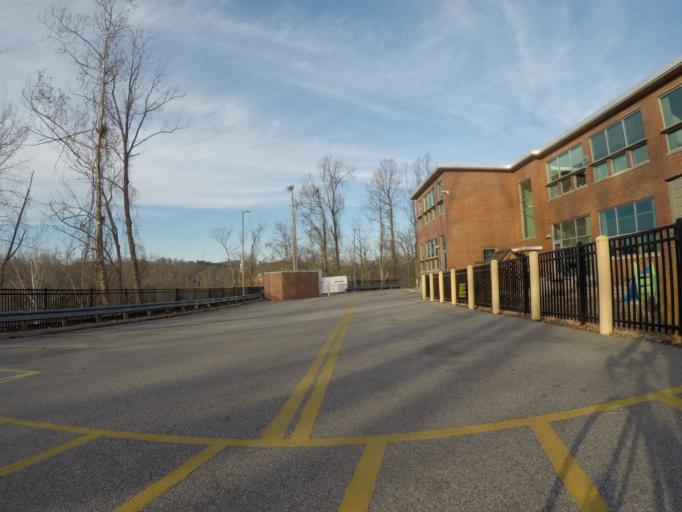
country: US
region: West Virginia
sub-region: Cabell County
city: Huntington
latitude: 38.4074
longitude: -82.3919
